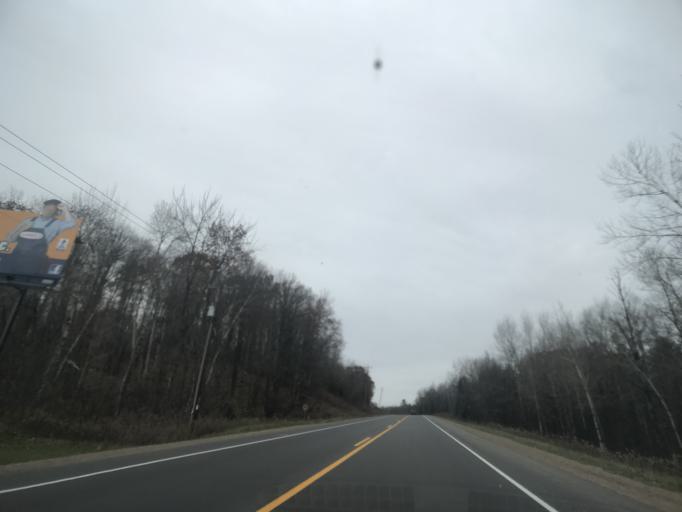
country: US
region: Wisconsin
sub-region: Menominee County
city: Legend Lake
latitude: 45.2854
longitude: -88.5100
